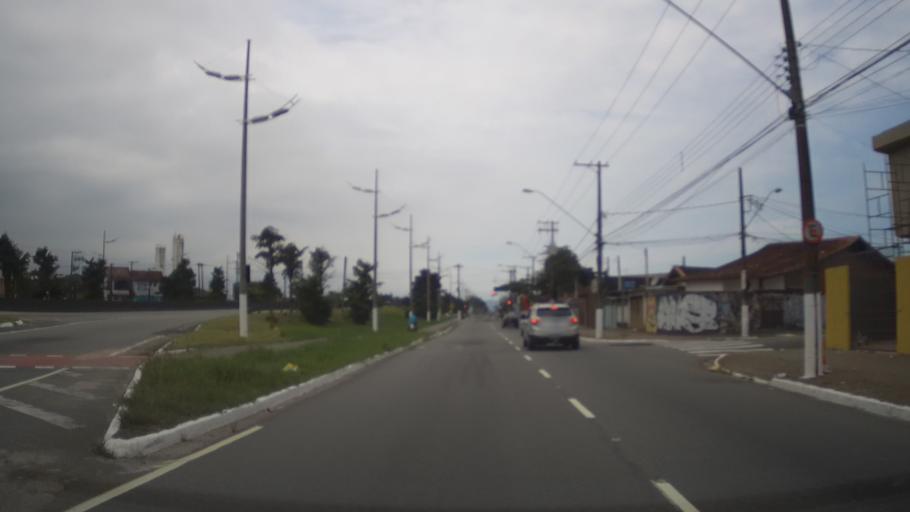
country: BR
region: Sao Paulo
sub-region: Praia Grande
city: Praia Grande
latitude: -24.0263
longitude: -46.4953
